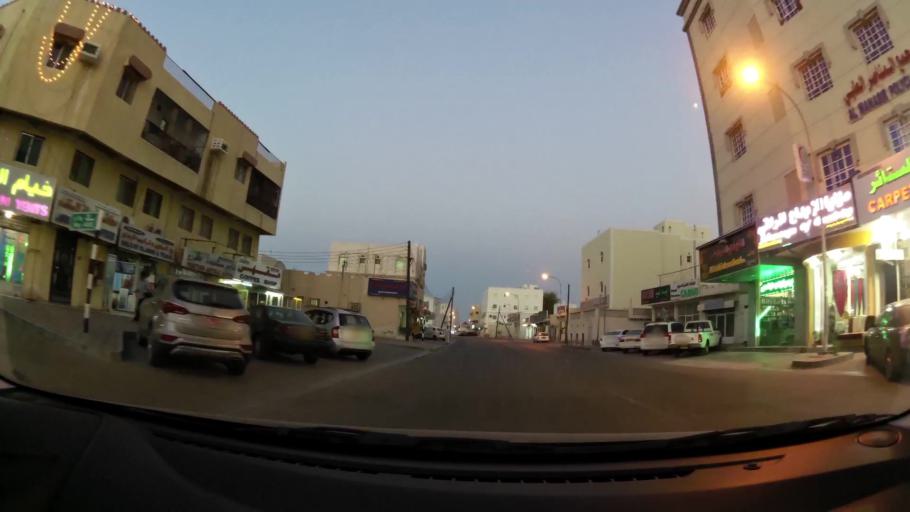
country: OM
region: Muhafazat Masqat
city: As Sib al Jadidah
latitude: 23.6830
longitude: 58.1781
